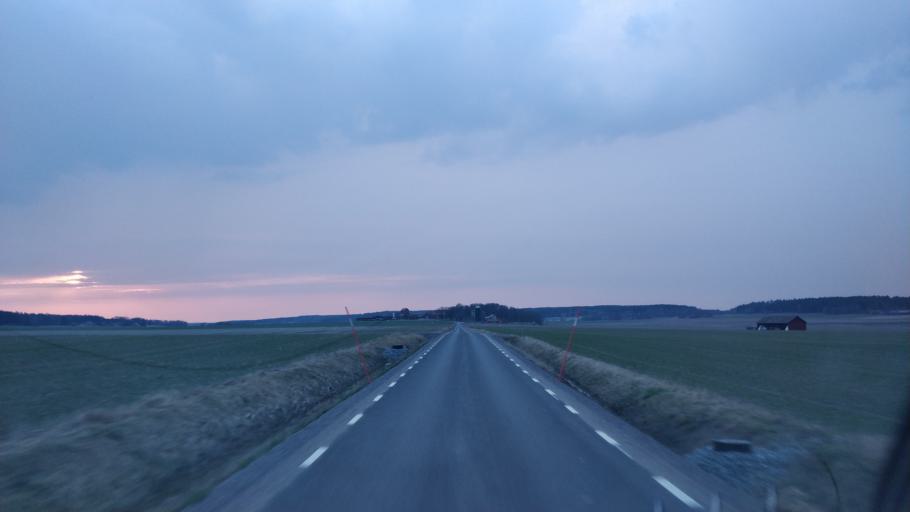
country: SE
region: Uppsala
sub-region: Enkopings Kommun
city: Orsundsbro
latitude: 59.7335
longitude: 17.1959
